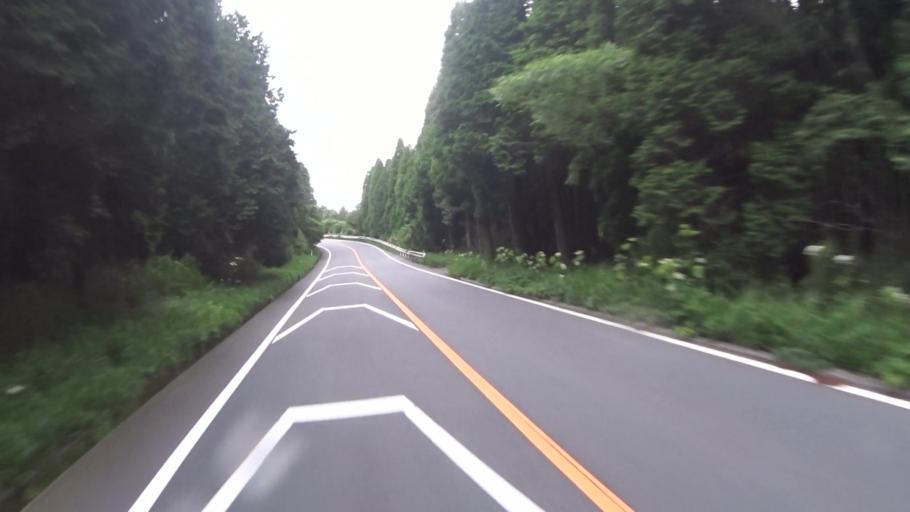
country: JP
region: Kumamoto
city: Ozu
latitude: 32.9177
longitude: 130.9667
